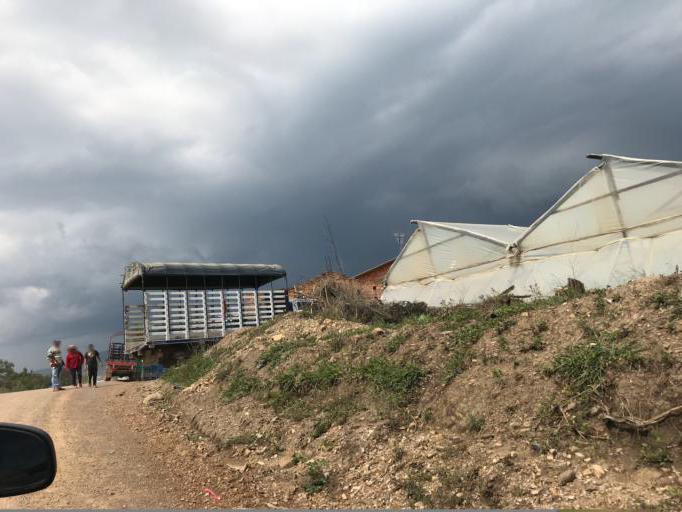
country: CO
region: Boyaca
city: Villa de Leiva
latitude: 5.6558
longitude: -73.5869
